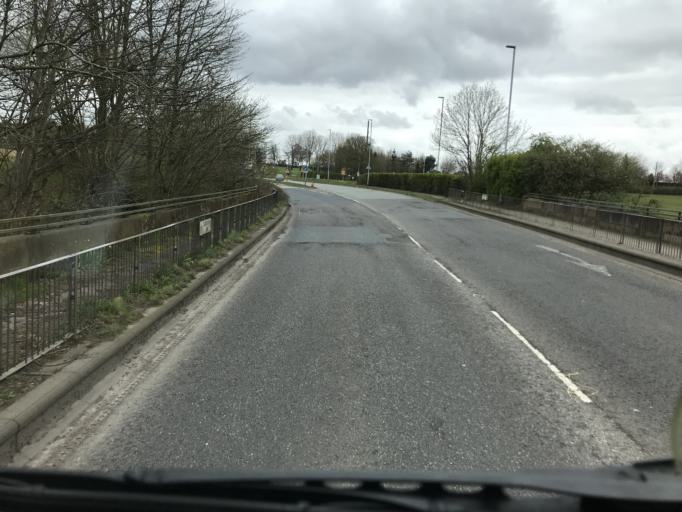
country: GB
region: England
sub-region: Trafford
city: Partington
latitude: 53.4181
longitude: -2.4507
